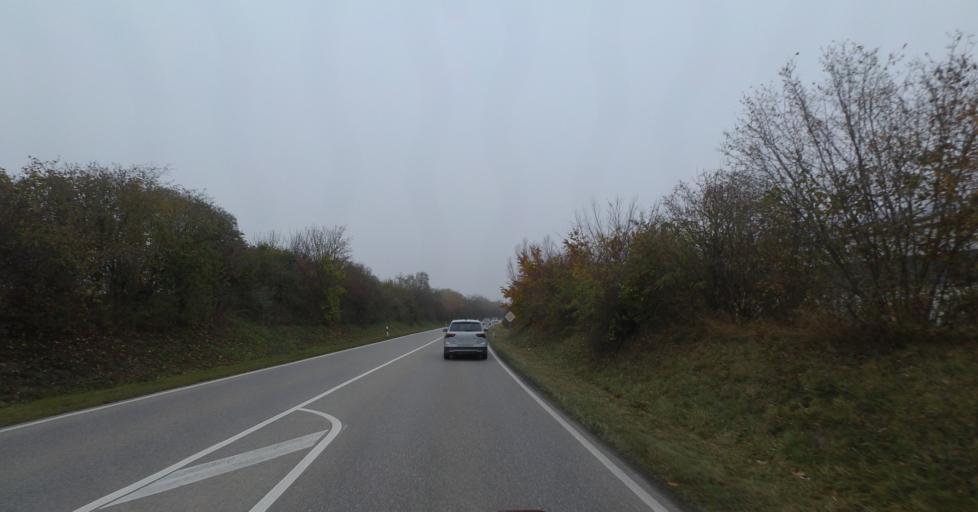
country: DE
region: Bavaria
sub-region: Upper Bavaria
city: Unterneukirchen
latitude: 48.1654
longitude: 12.6120
